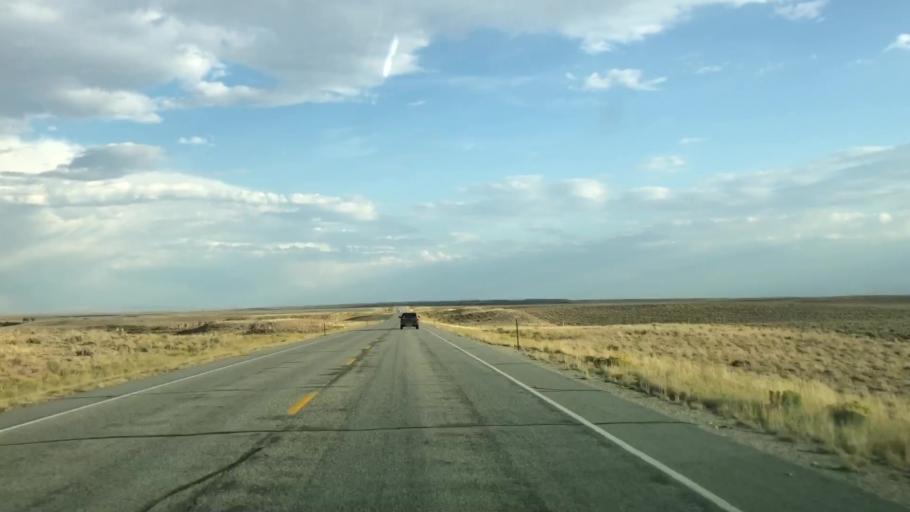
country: US
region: Wyoming
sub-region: Sublette County
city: Marbleton
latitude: 42.3309
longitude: -109.5161
